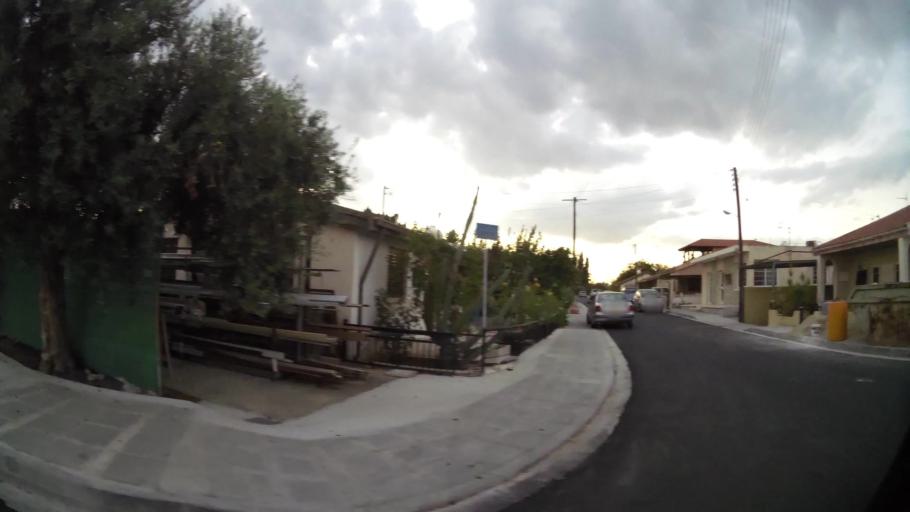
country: CY
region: Larnaka
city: Dhromolaxia
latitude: 34.8723
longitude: 33.5855
